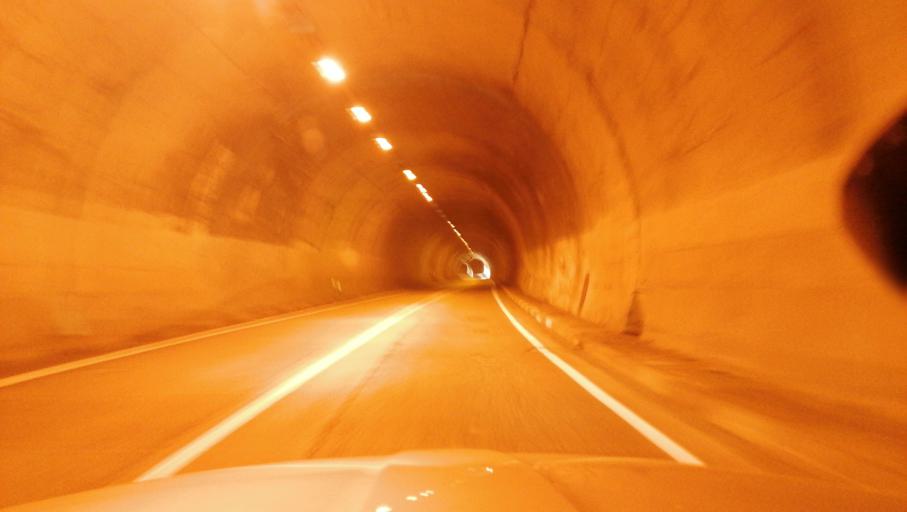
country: BA
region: Republika Srpska
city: Cajnice
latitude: 43.6854
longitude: 19.1535
